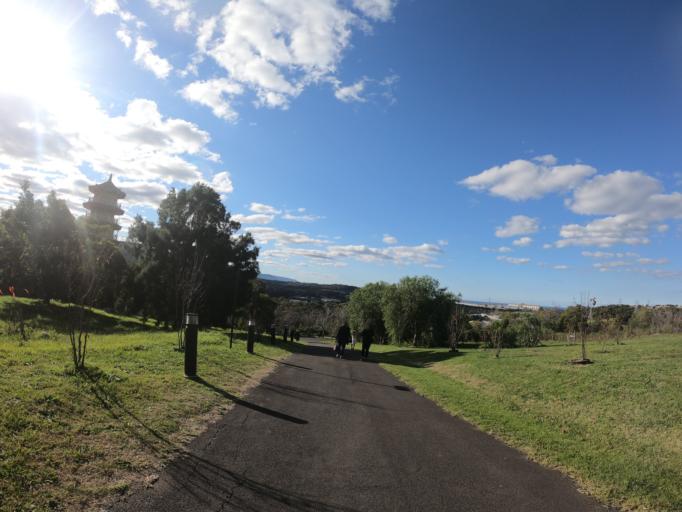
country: AU
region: New South Wales
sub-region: Wollongong
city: Berkeley
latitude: -34.4667
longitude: 150.8508
